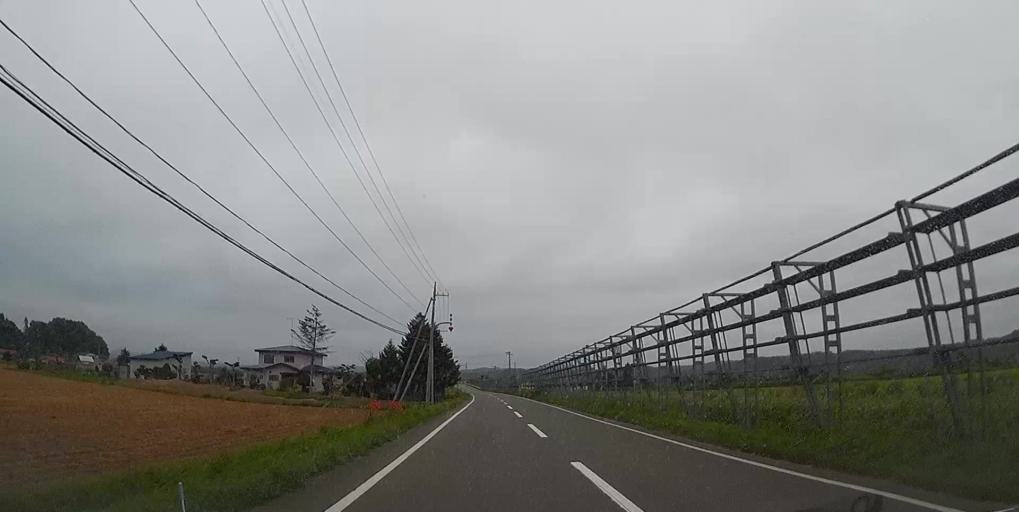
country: JP
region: Hokkaido
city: Iwanai
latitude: 42.4008
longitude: 140.0053
